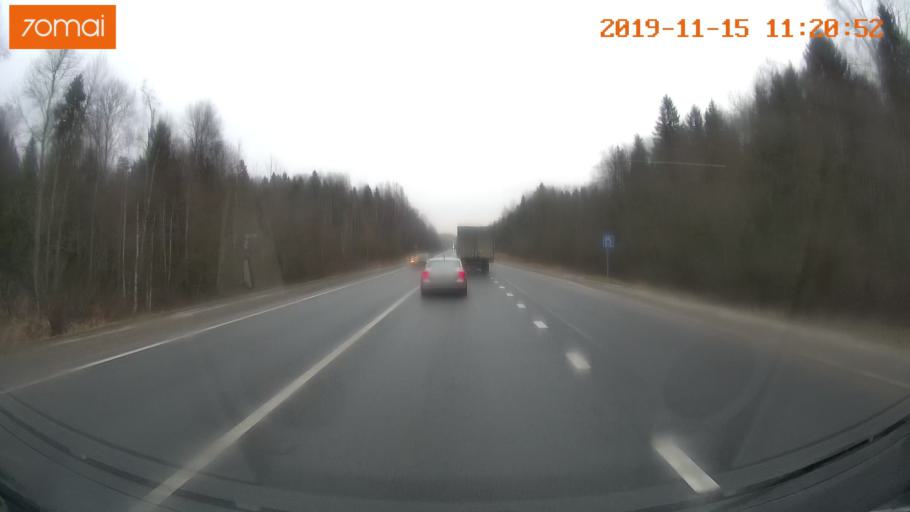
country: RU
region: Vologda
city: Molochnoye
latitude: 59.1428
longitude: 39.3244
